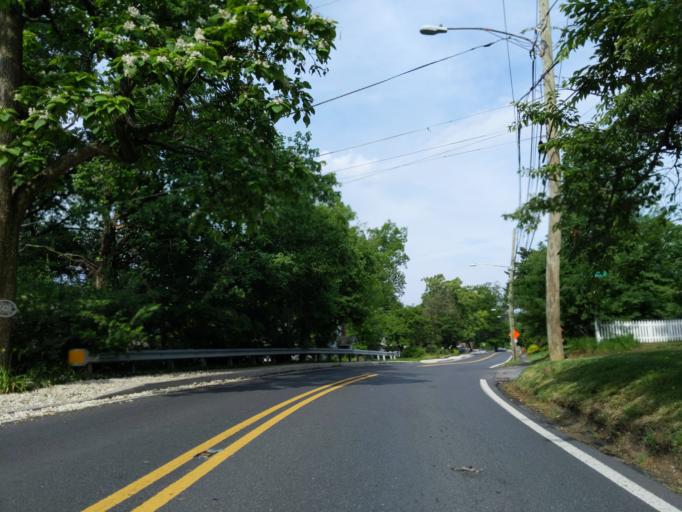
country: US
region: Maryland
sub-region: Montgomery County
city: Forest Glen
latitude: 39.0146
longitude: -77.0515
